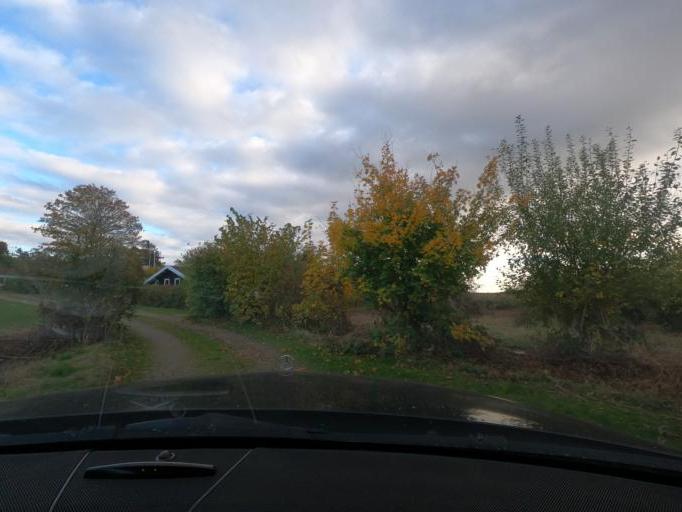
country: DK
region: South Denmark
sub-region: Sonderborg Kommune
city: Horuphav
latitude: 54.8701
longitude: 9.8863
